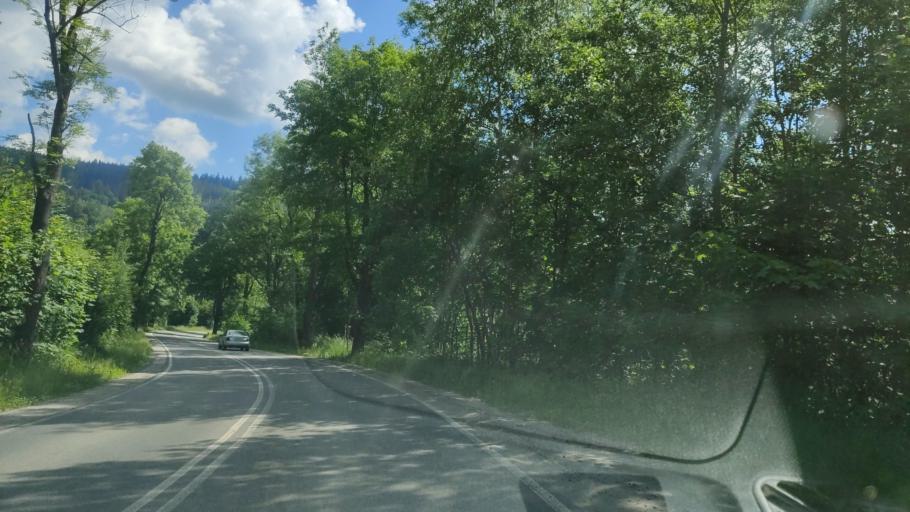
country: PL
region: Lower Silesian Voivodeship
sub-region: Powiat jeleniogorski
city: Kowary
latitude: 50.7762
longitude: 15.9105
